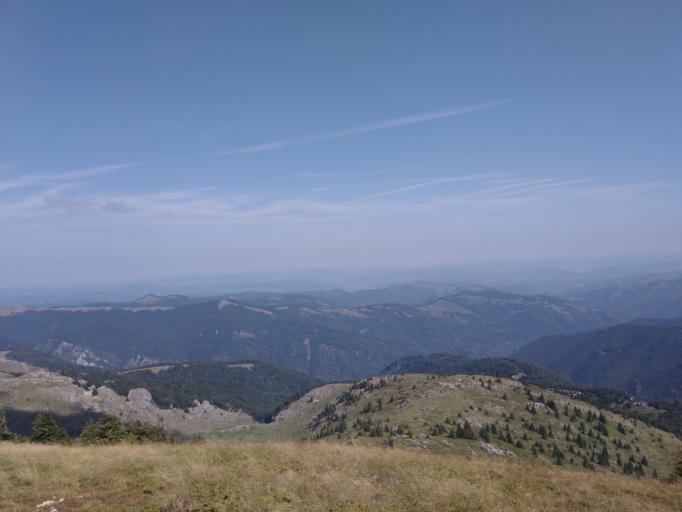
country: BG
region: Plovdiv
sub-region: Obshtina Karlovo
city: Karlovo
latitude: 42.7308
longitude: 24.7435
